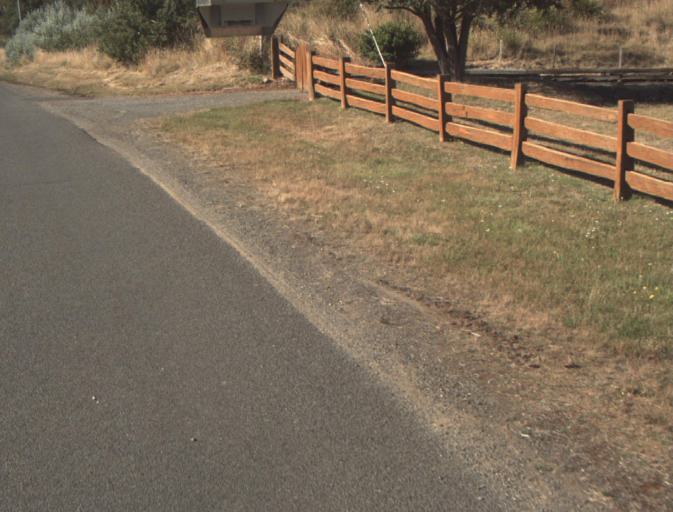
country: AU
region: Tasmania
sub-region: Launceston
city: Newstead
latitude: -41.3888
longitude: 147.2966
